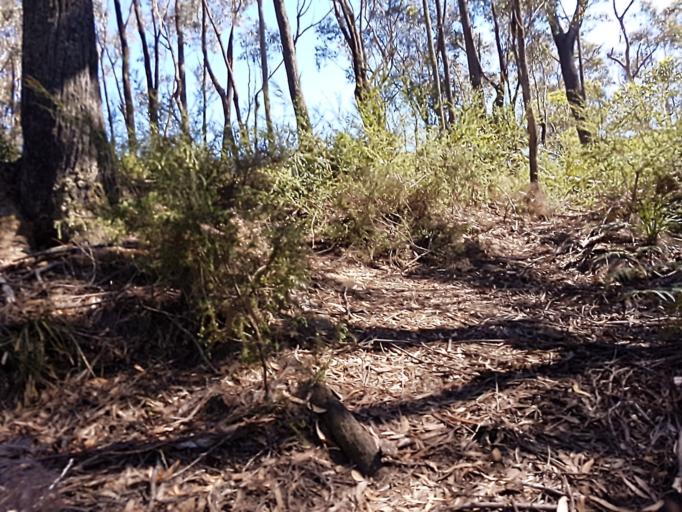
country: AU
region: Victoria
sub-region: East Gippsland
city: Lakes Entrance
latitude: -37.2204
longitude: 148.2817
